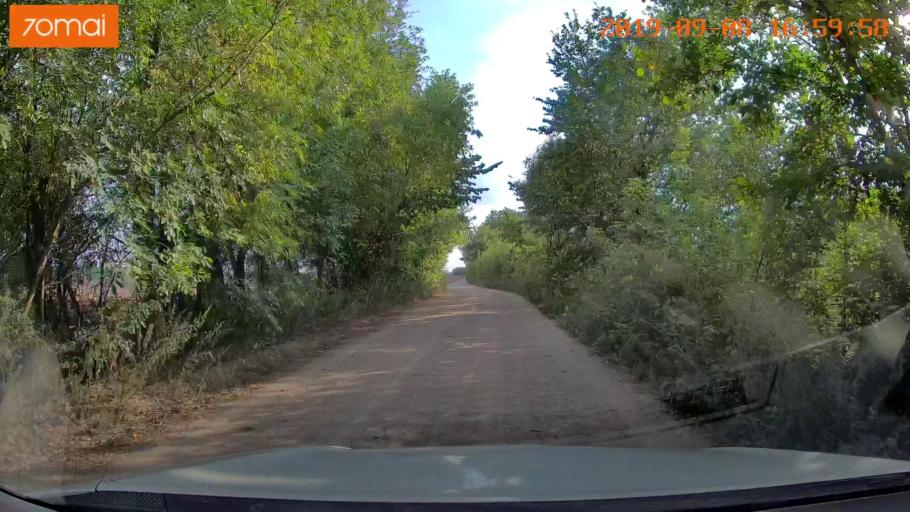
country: BY
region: Grodnenskaya
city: Hrodna
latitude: 53.7194
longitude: 23.9329
